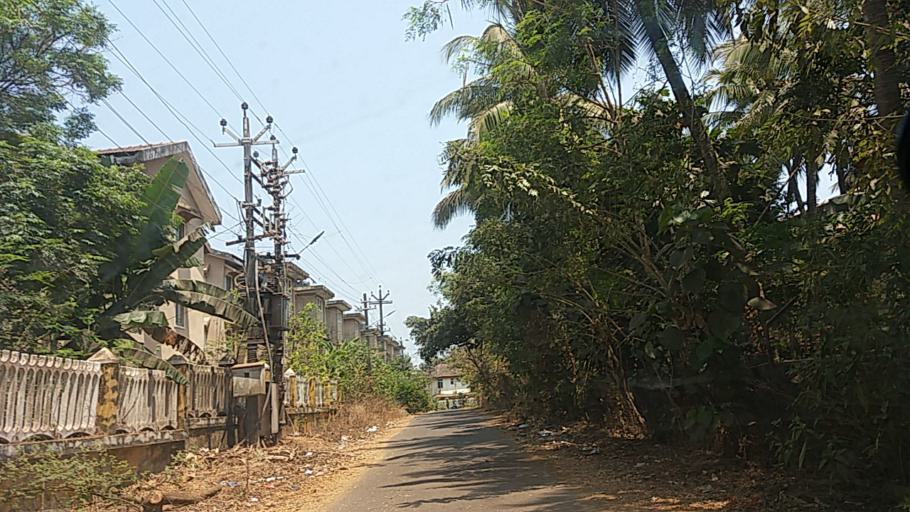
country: IN
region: Goa
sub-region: North Goa
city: Serula
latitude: 15.5242
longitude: 73.8327
